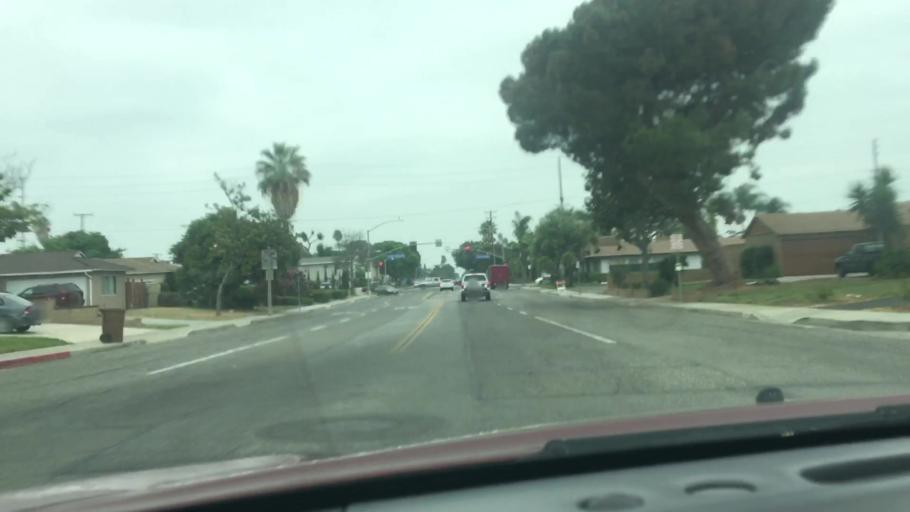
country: US
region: California
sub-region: Orange County
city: Placentia
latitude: 33.8706
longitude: -117.8880
